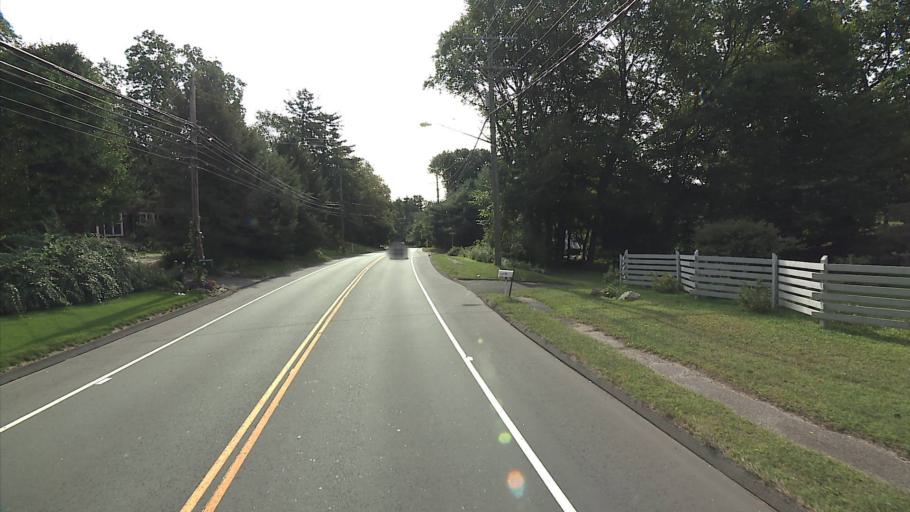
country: US
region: Connecticut
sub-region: Fairfield County
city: Norwalk
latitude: 41.1310
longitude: -73.4433
